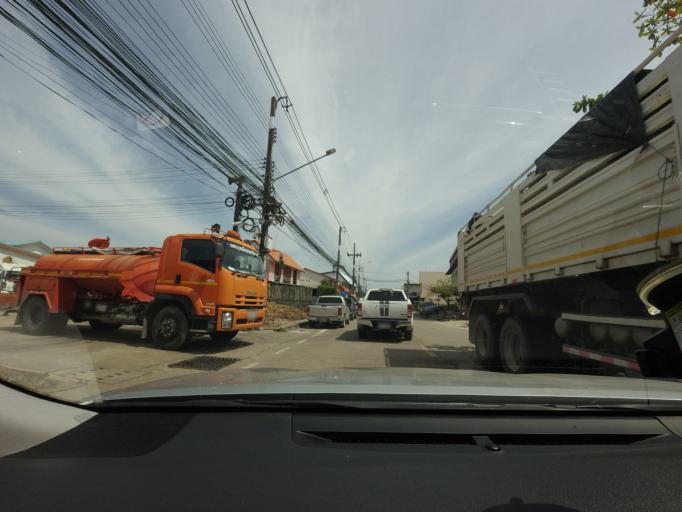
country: TH
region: Narathiwat
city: Narathiwat
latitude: 6.4242
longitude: 101.8147
